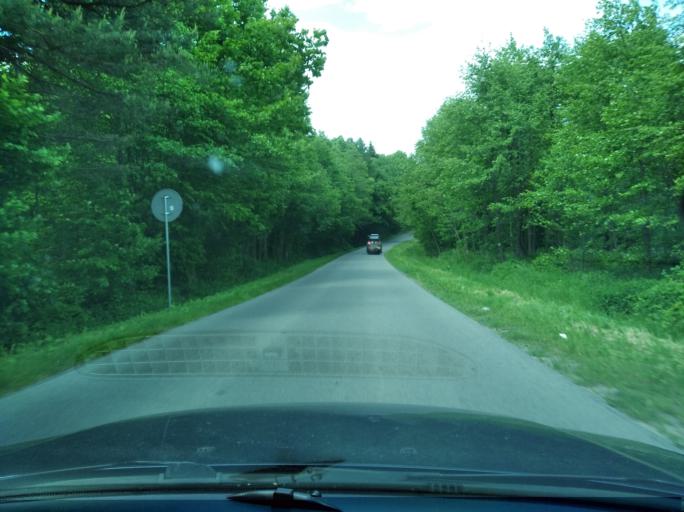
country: PL
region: Subcarpathian Voivodeship
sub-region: Powiat ropczycko-sedziszowski
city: Ropczyce
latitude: 50.0178
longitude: 21.6087
